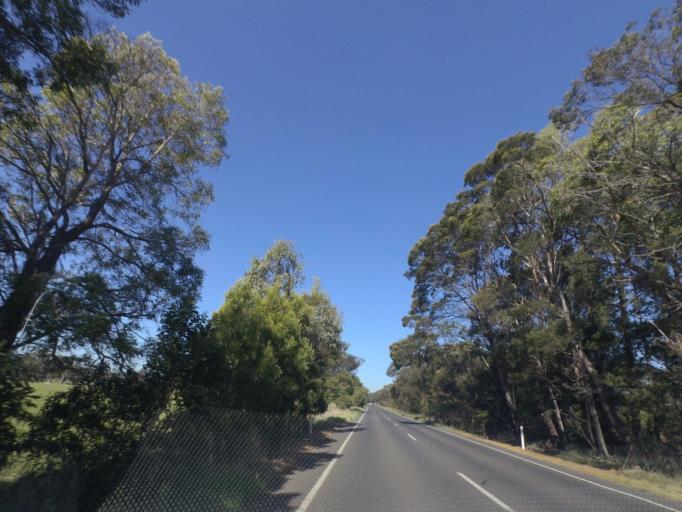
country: AU
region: Victoria
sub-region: Whittlesea
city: Whittlesea
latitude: -37.3270
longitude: 144.9736
